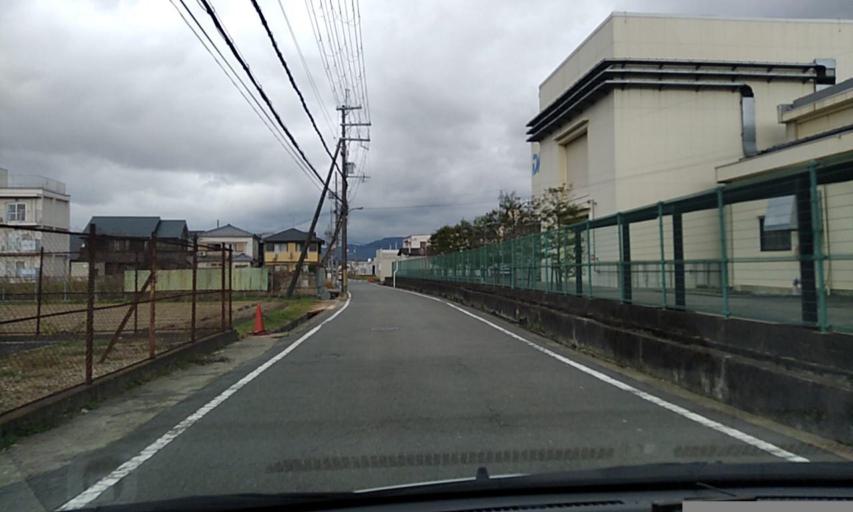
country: JP
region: Kyoto
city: Kameoka
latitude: 35.0213
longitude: 135.5636
